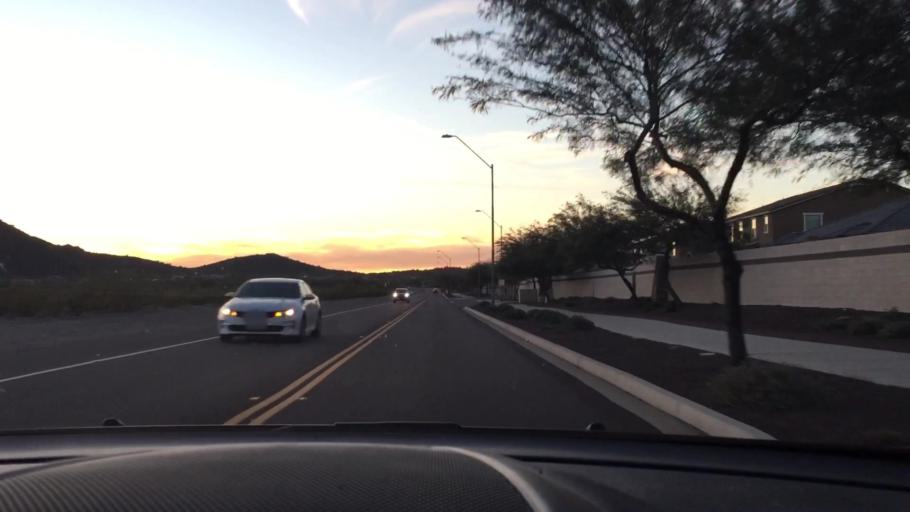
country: US
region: Arizona
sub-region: Maricopa County
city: Sun City West
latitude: 33.7251
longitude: -112.2301
